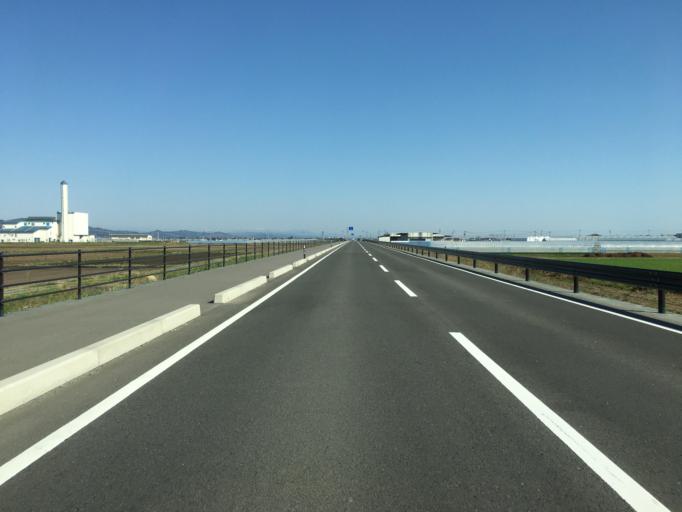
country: JP
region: Miyagi
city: Watari
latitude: 37.9520
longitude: 140.9055
